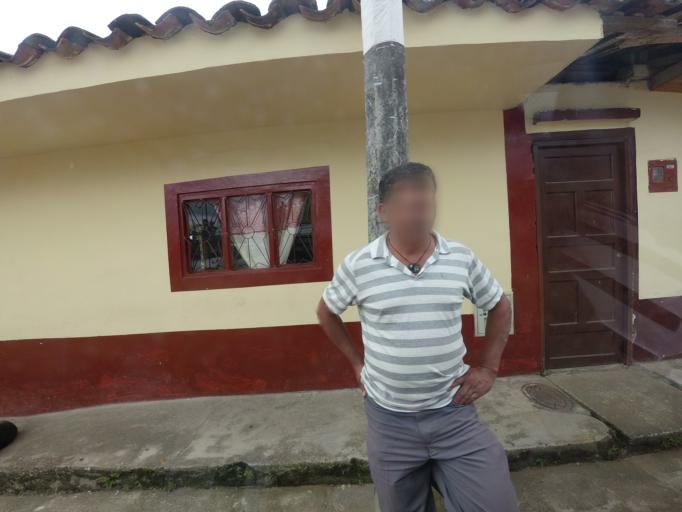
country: CO
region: Huila
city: San Agustin
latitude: 1.9394
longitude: -76.2985
